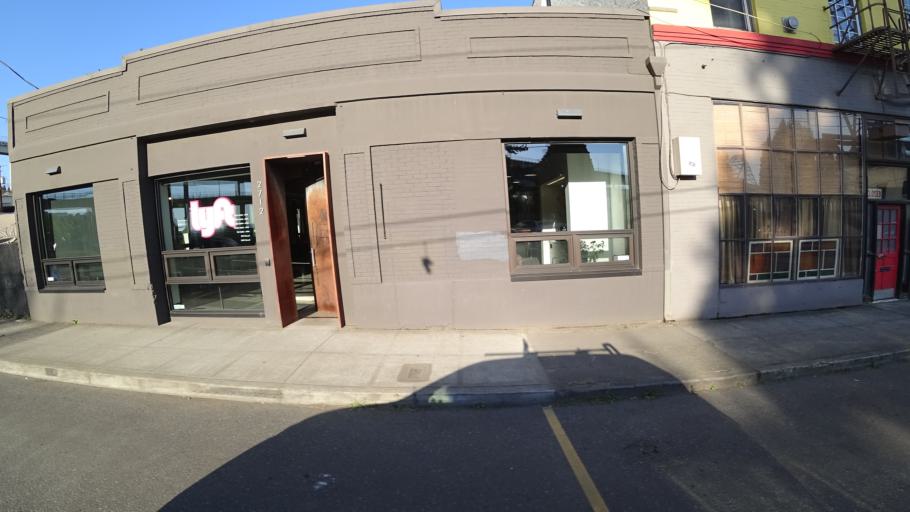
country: US
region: Oregon
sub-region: Multnomah County
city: Portland
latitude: 45.5422
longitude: -122.6759
